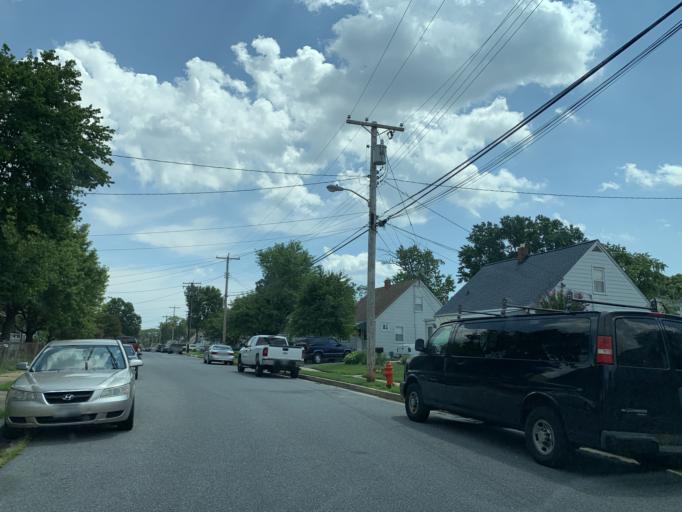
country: US
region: Maryland
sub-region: Baltimore County
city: Essex
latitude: 39.3034
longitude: -76.4614
